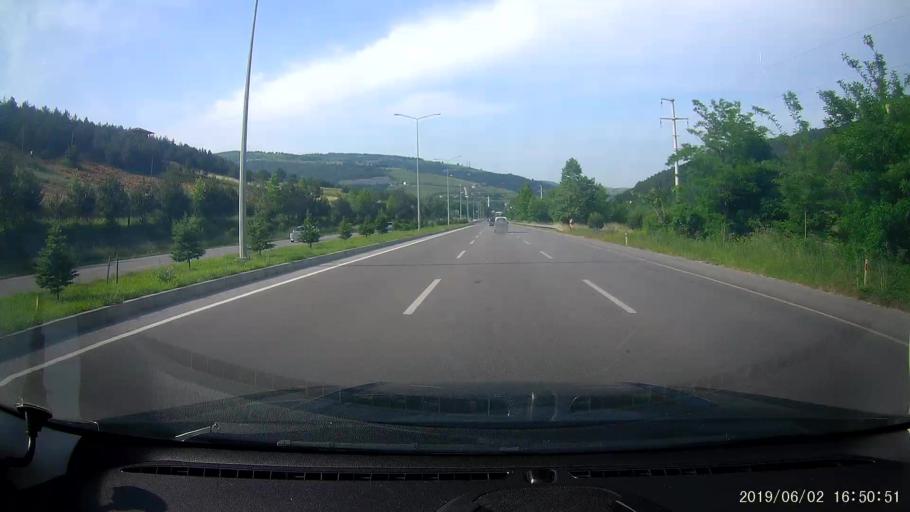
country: TR
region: Samsun
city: Taflan
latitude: 41.2634
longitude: 36.1761
